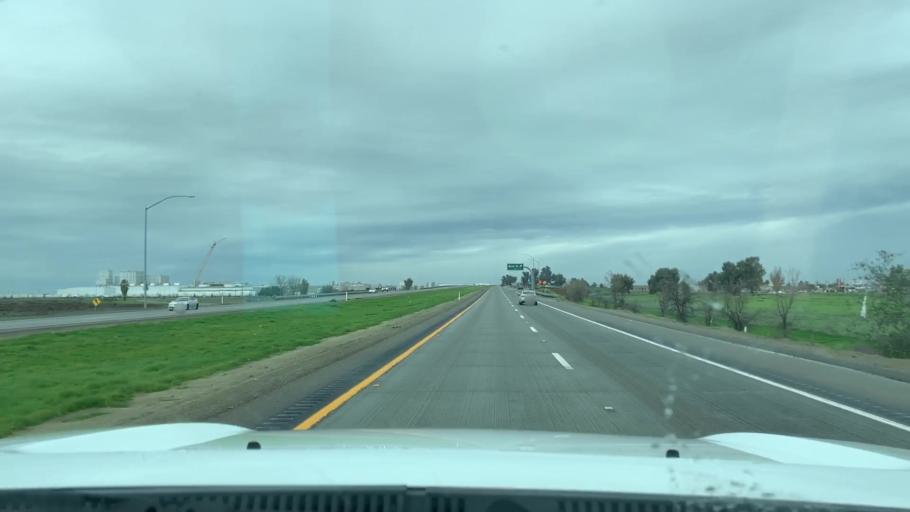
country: US
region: California
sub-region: Kings County
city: Lemoore
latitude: 36.2914
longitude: -119.8087
